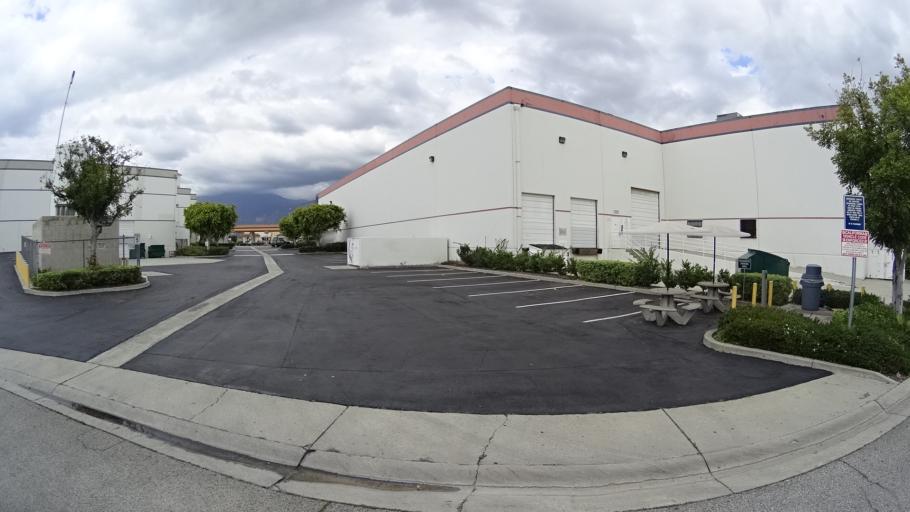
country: US
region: California
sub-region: Los Angeles County
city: Baldwin Park
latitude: 34.1055
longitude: -117.9739
